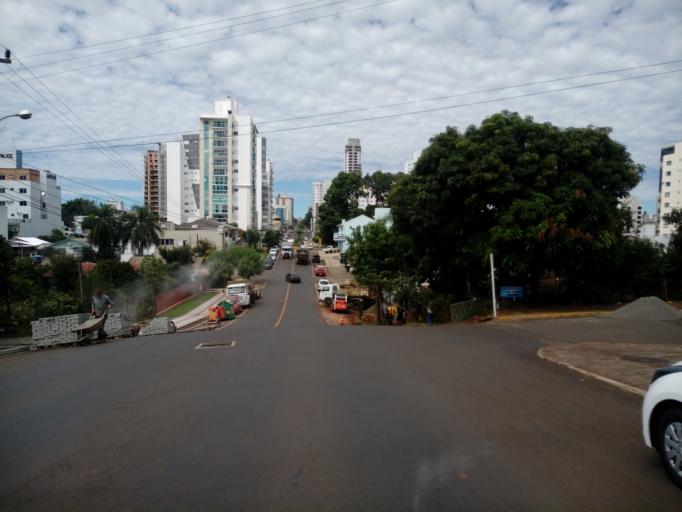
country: BR
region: Santa Catarina
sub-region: Chapeco
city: Chapeco
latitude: -27.0963
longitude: -52.6100
